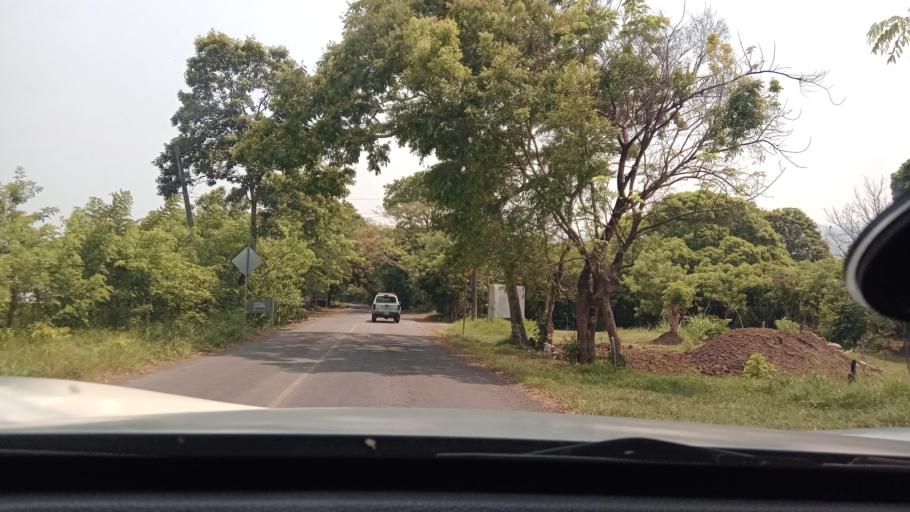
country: MX
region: Veracruz
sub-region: San Andres Tuxtla
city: Santa Rosa Abata
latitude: 18.5564
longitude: -95.0602
